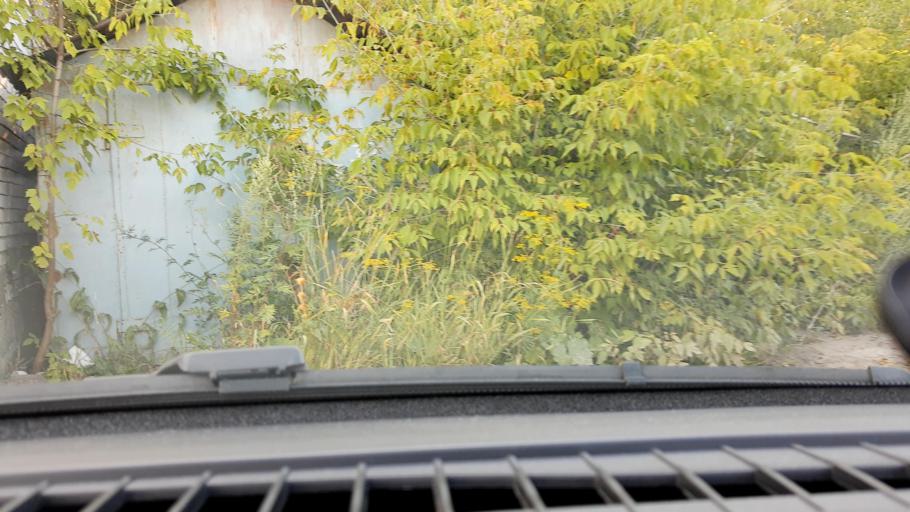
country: RU
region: Nizjnij Novgorod
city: Gorbatovka
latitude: 56.2500
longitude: 43.8242
